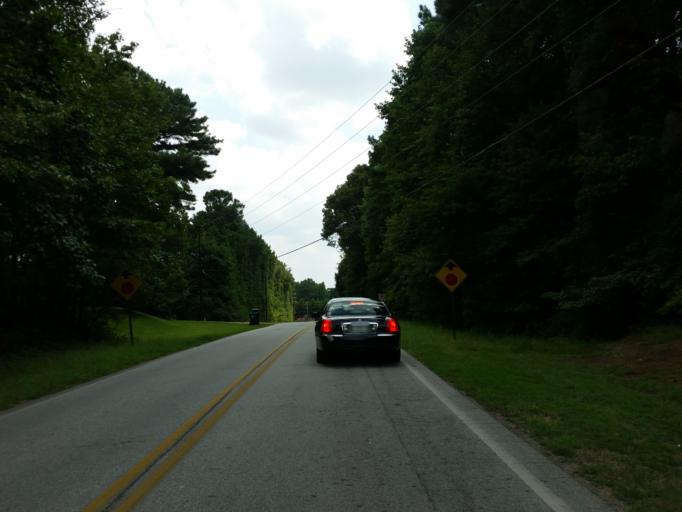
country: US
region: Georgia
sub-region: Henry County
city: Stockbridge
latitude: 33.5115
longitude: -84.2778
